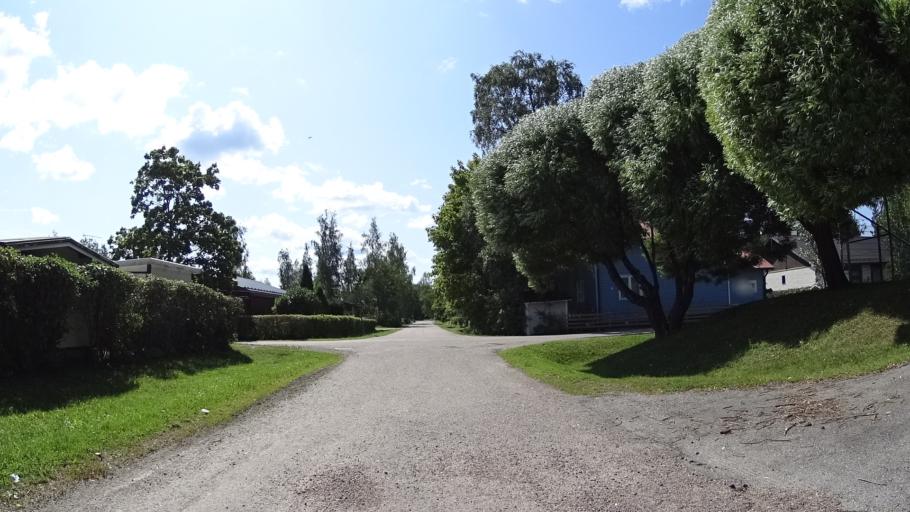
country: FI
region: Uusimaa
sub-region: Helsinki
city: Jaervenpaeae
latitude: 60.4728
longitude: 25.0781
